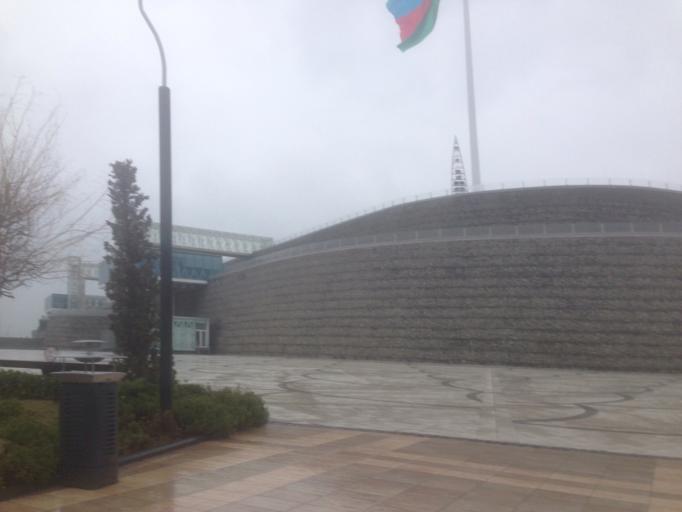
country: AZ
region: Baki
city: Badamdar
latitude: 40.3462
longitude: 49.8455
